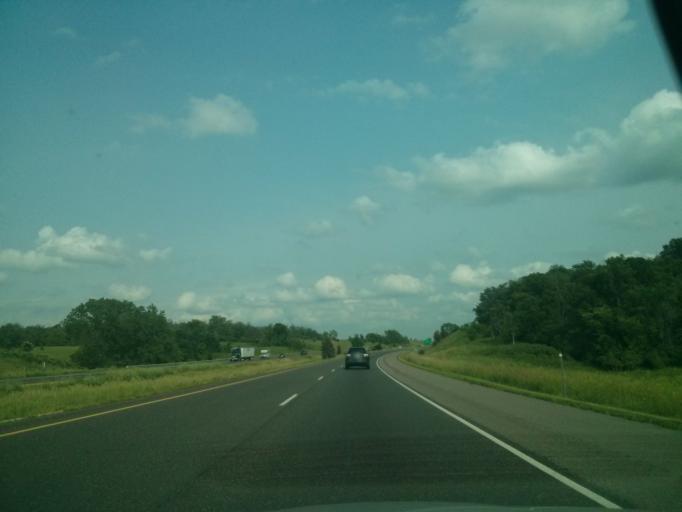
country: US
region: Wisconsin
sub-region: Saint Croix County
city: Roberts
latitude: 44.9632
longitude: -92.6241
